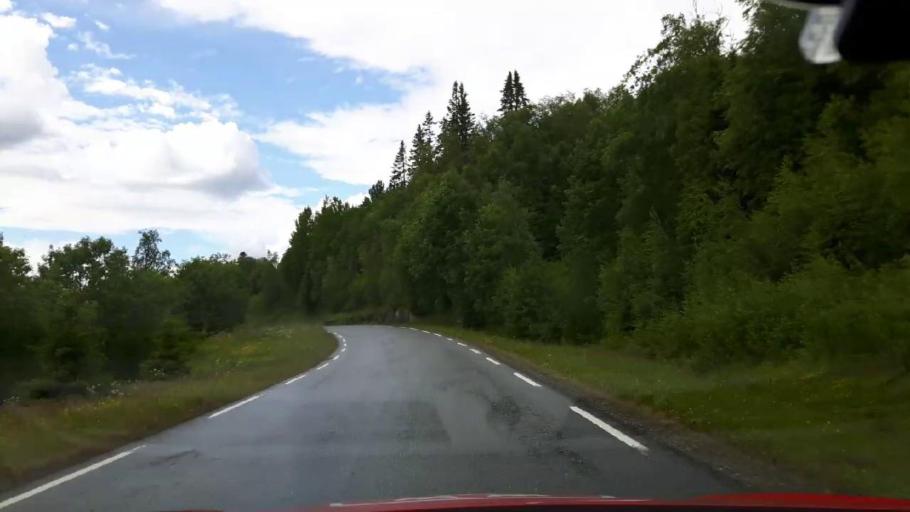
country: NO
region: Nord-Trondelag
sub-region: Lierne
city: Sandvika
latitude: 64.1054
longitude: 13.9916
